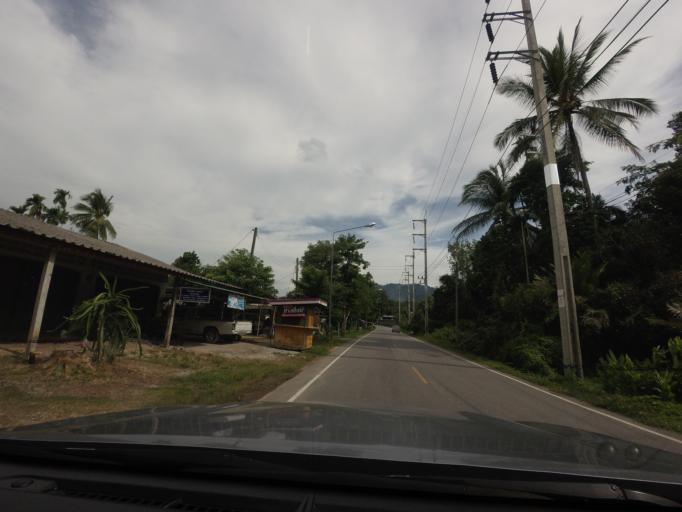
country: TH
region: Yala
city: Yala
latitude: 6.5107
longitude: 101.2882
